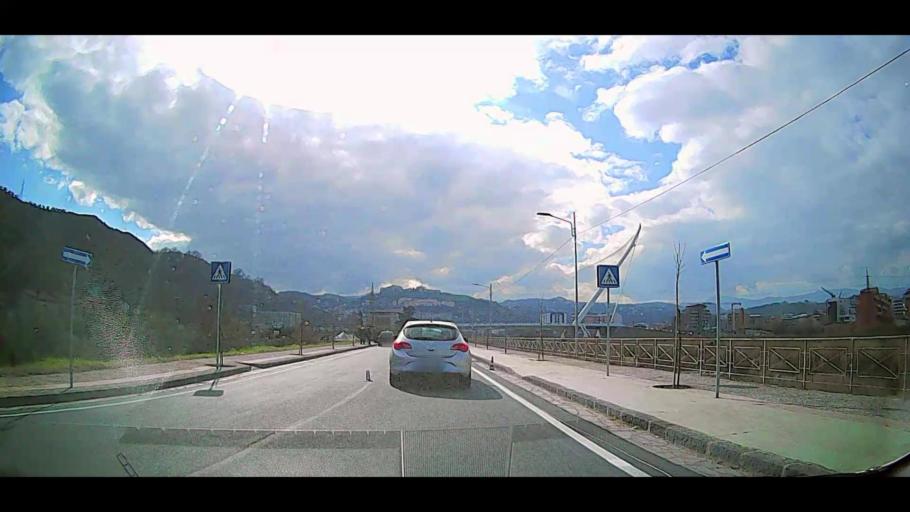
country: IT
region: Calabria
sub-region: Provincia di Cosenza
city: Cosenza
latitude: 39.3013
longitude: 16.2627
